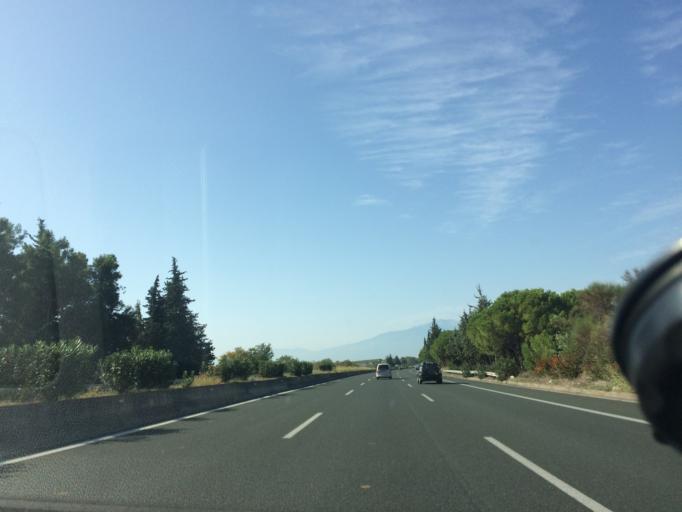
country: GR
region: Central Macedonia
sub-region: Nomos Pierias
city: Kitros
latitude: 40.3632
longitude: 22.6032
